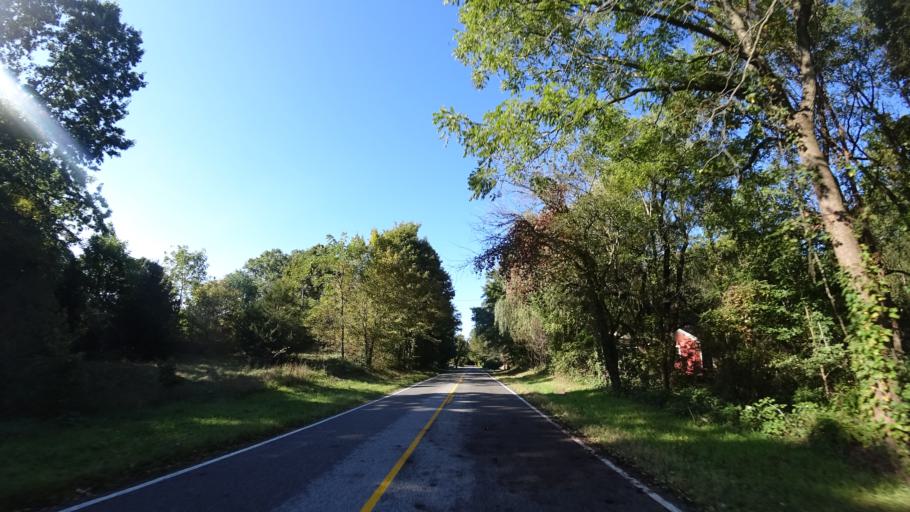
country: US
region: Michigan
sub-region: Berrien County
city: Benton Heights
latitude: 42.1563
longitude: -86.4167
